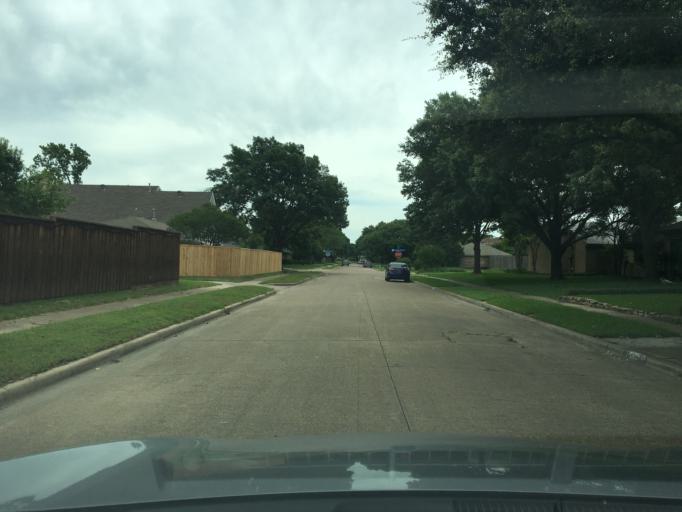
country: US
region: Texas
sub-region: Dallas County
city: Richardson
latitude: 32.9337
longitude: -96.7091
